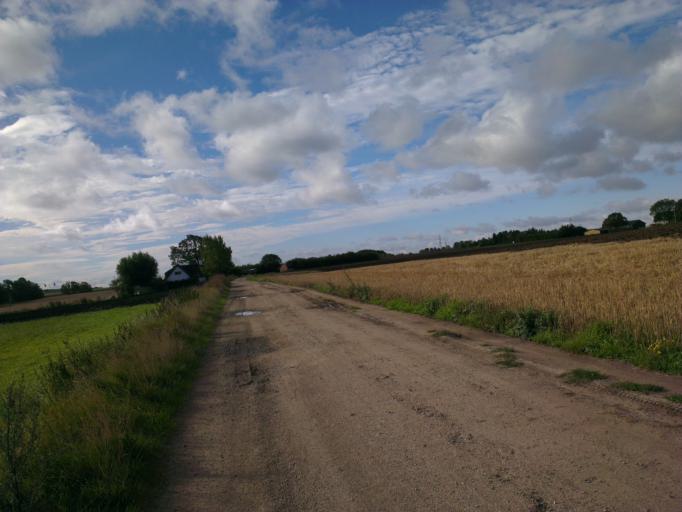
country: DK
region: Capital Region
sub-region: Frederikssund Kommune
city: Frederikssund
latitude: 55.8047
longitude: 12.0856
